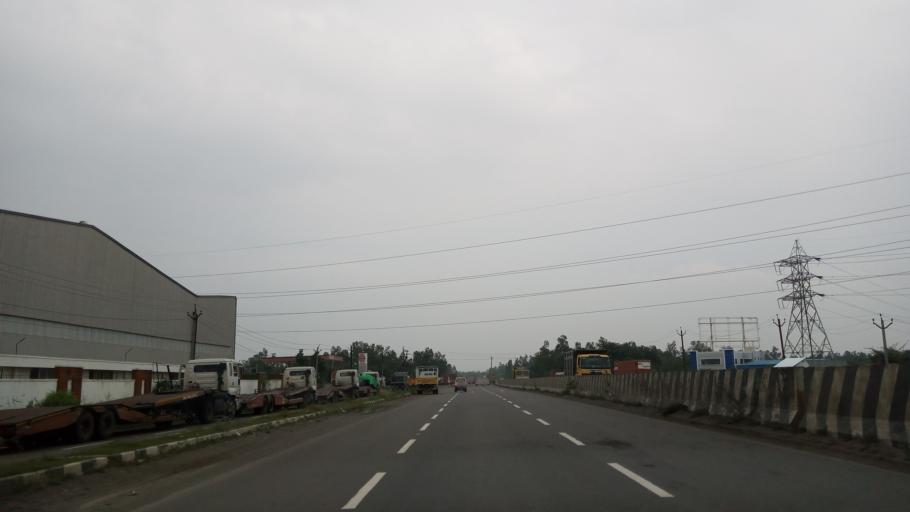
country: IN
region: Tamil Nadu
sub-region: Kancheepuram
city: Madambakkam
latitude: 12.8548
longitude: 79.9495
